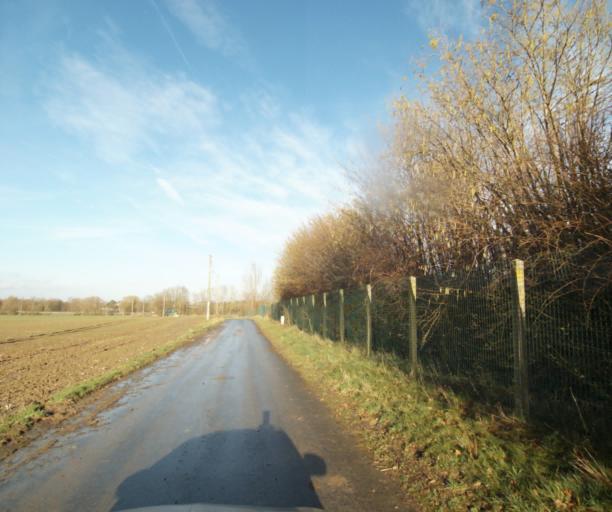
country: FR
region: Nord-Pas-de-Calais
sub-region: Departement du Nord
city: Curgies
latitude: 50.3193
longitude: 3.6011
